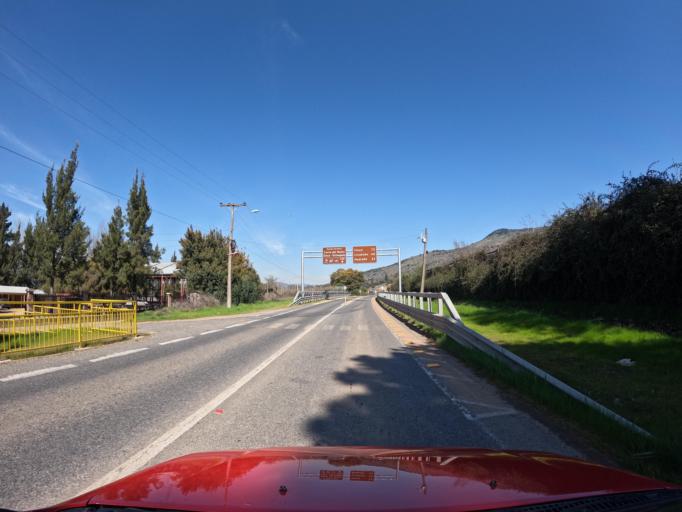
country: CL
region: Maule
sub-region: Provincia de Curico
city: Rauco
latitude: -35.0620
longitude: -71.6193
